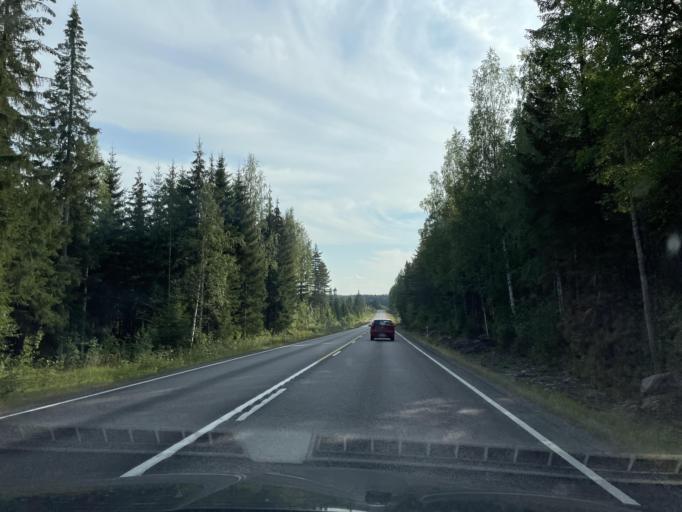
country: FI
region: Central Finland
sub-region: Jaemsae
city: Kuhmoinen
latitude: 61.6140
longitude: 25.2663
